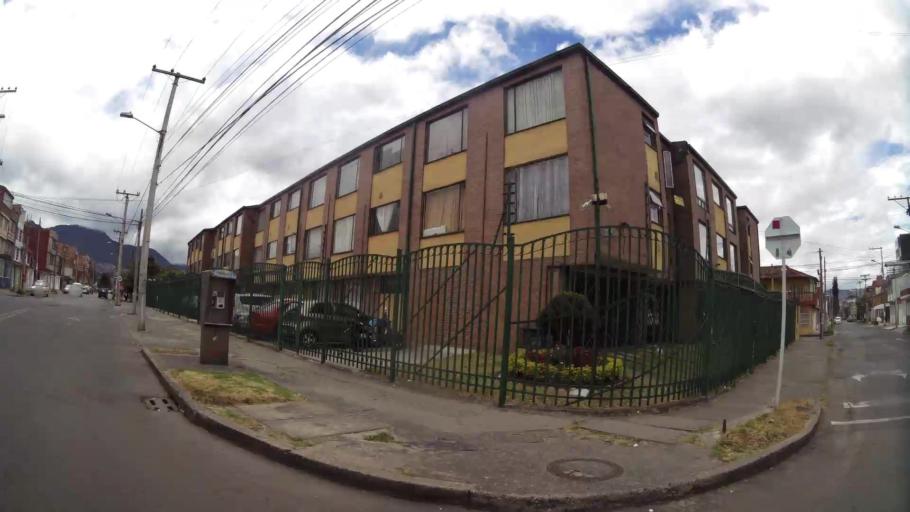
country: CO
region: Bogota D.C.
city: Bogota
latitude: 4.6084
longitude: -74.1102
